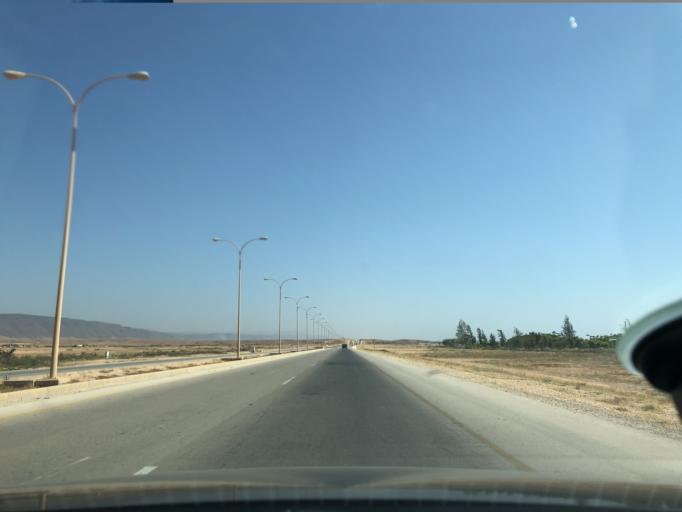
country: OM
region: Zufar
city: Salalah
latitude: 17.0524
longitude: 54.2942
